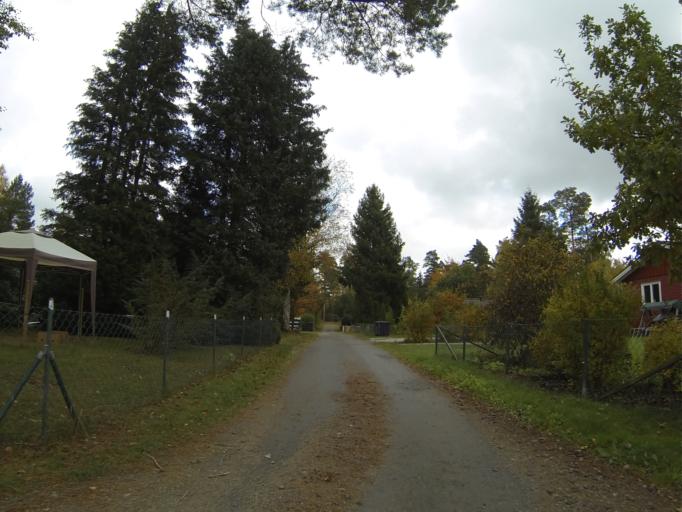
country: SE
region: Skane
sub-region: Sjobo Kommun
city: Sjoebo
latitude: 55.6317
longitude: 13.6485
